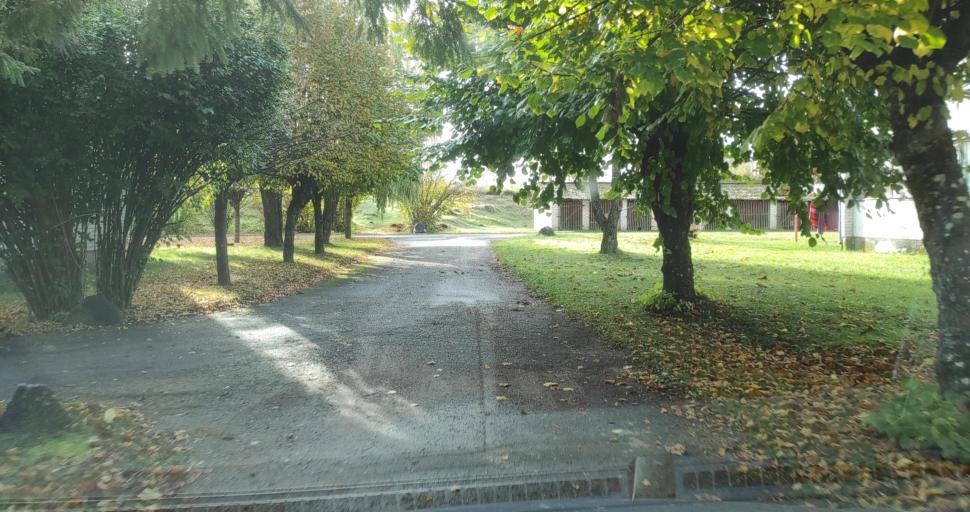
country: LV
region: Skrunda
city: Skrunda
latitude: 56.6826
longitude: 22.0494
